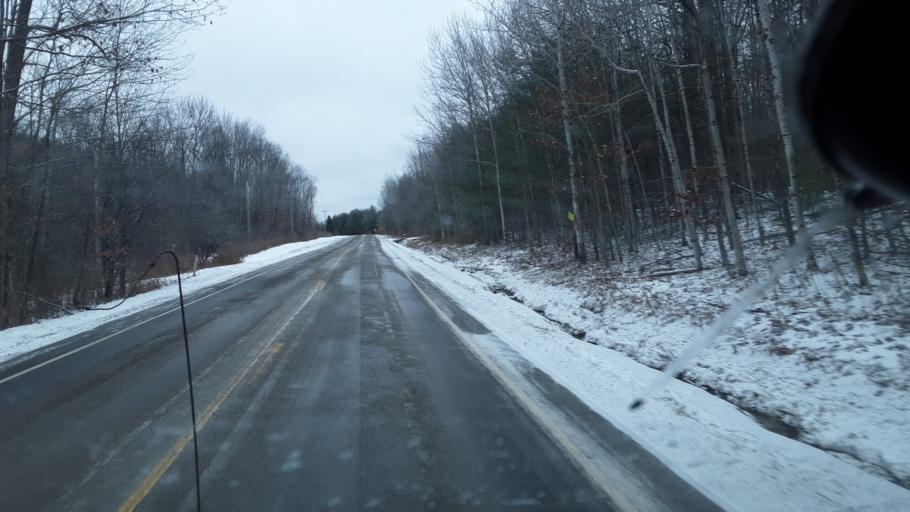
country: US
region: New York
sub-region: Allegany County
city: Friendship
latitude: 42.2242
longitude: -78.1415
